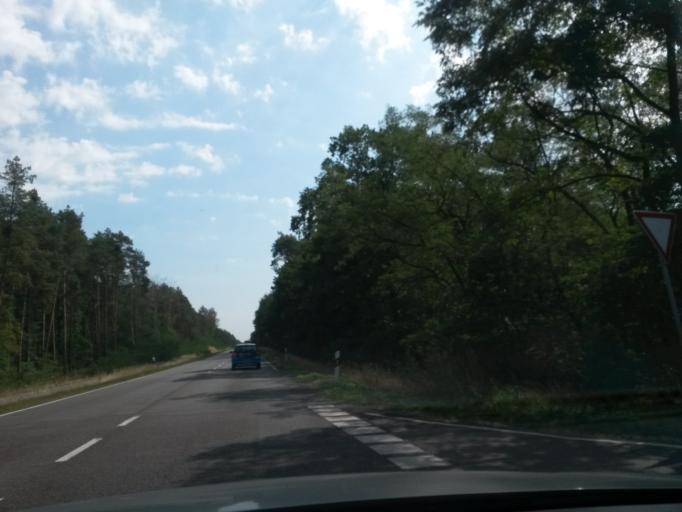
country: DE
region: Saxony-Anhalt
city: Jerichow
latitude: 52.4923
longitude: 12.0325
